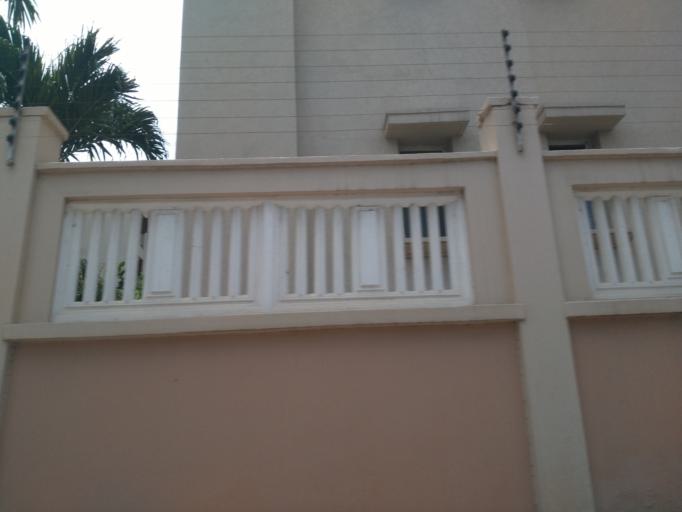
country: TZ
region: Dar es Salaam
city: Magomeni
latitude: -6.7510
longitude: 39.2416
